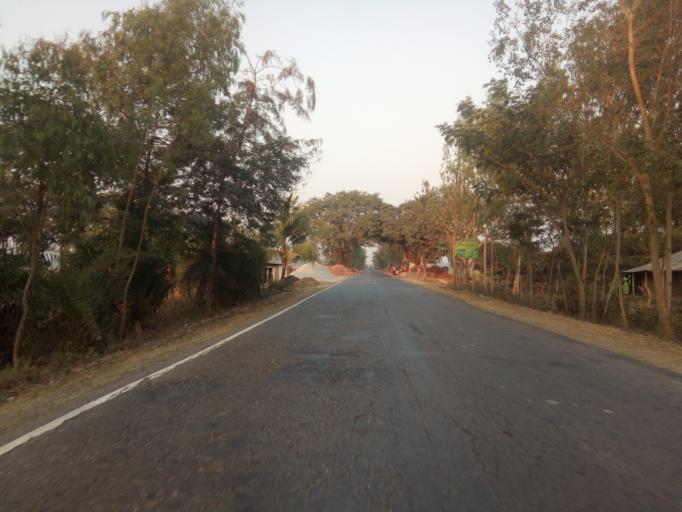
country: BD
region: Rajshahi
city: Bogra
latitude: 24.5773
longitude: 89.2213
